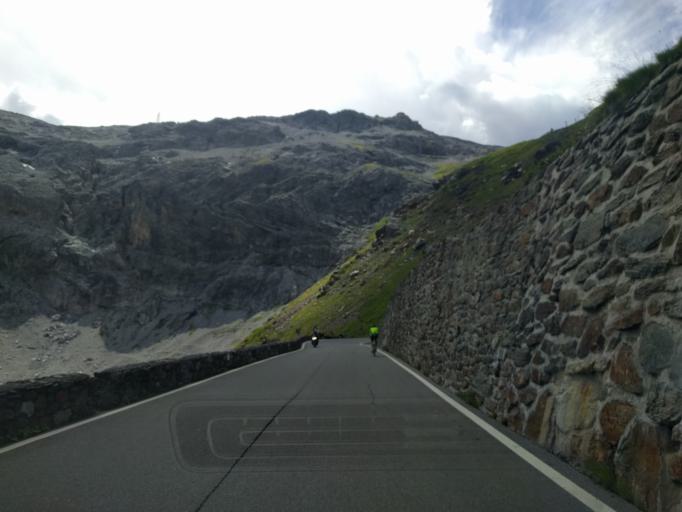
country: IT
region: Lombardy
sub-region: Provincia di Sondrio
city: Sant'Antonio
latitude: 46.5315
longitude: 10.4618
